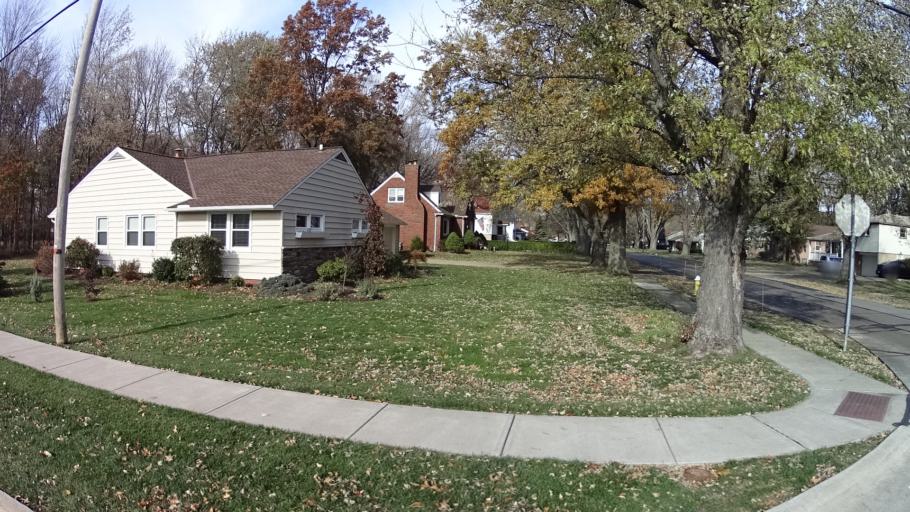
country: US
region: Ohio
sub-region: Lorain County
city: Avon Lake
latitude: 41.4975
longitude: -82.0396
